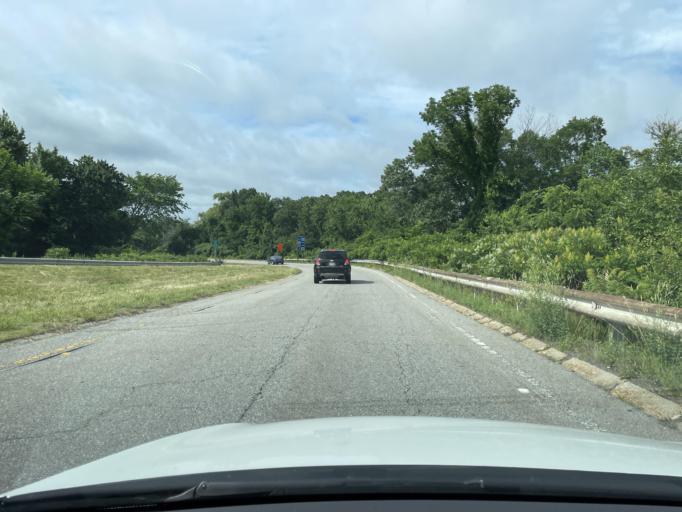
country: US
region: Massachusetts
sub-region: Middlesex County
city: Stoneham
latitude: 42.4816
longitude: -71.1172
